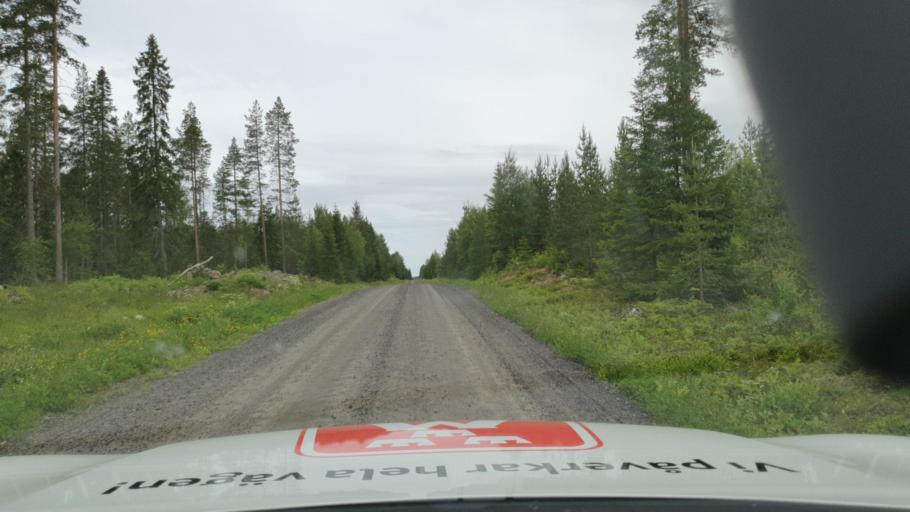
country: SE
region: Vaesterbotten
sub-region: Skelleftea Kommun
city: Burtraesk
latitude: 64.3683
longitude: 20.6165
